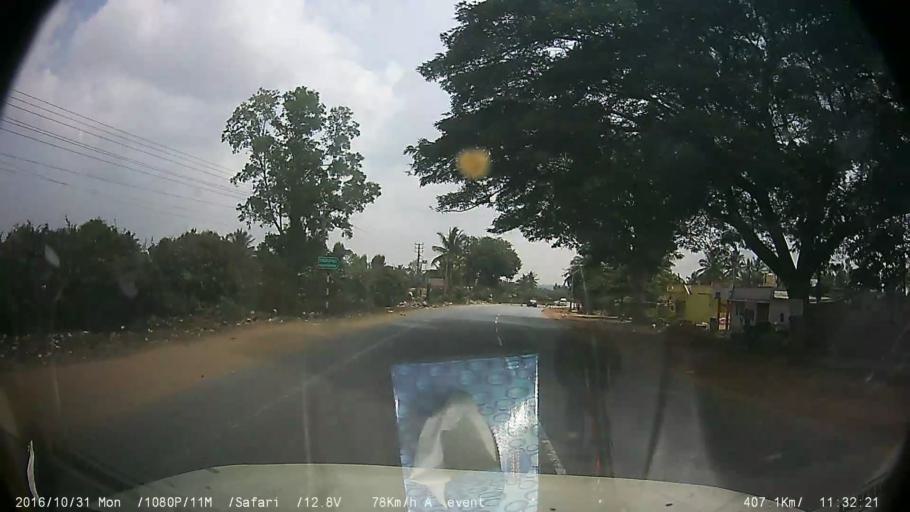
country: IN
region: Karnataka
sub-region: Mysore
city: Hunsur
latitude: 12.3137
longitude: 76.2509
